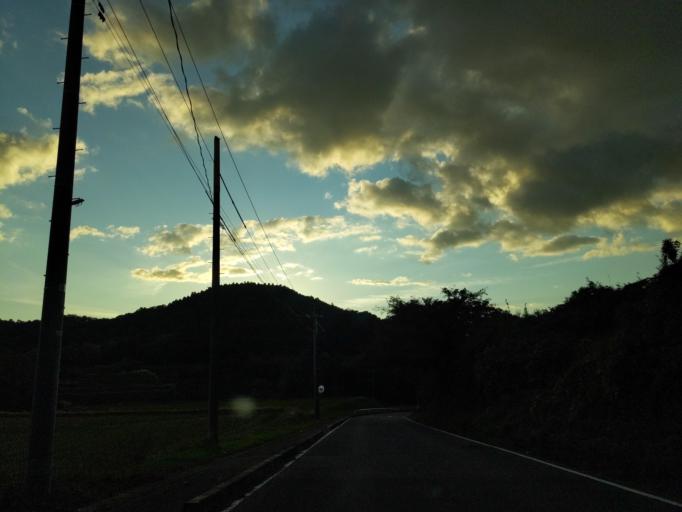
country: JP
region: Fukushima
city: Motomiya
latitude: 37.4784
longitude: 140.4037
